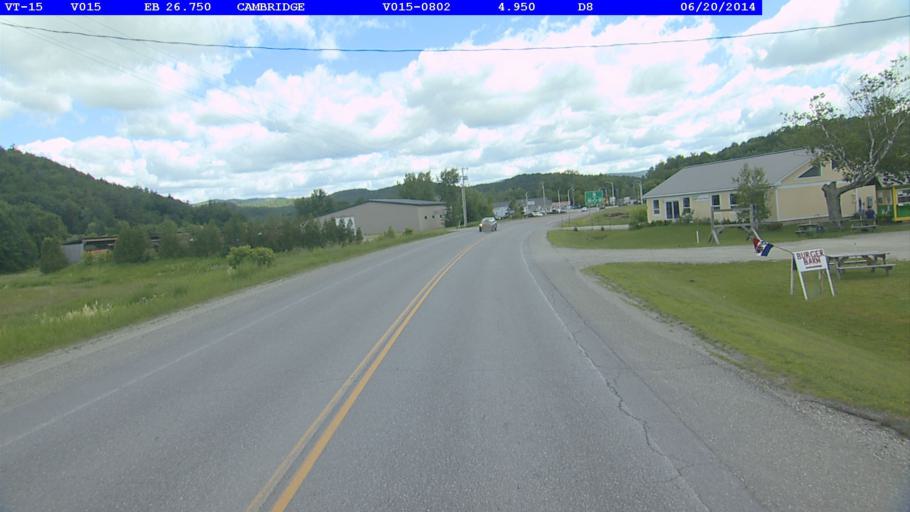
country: US
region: Vermont
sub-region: Lamoille County
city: Johnson
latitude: 44.6463
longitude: -72.8323
